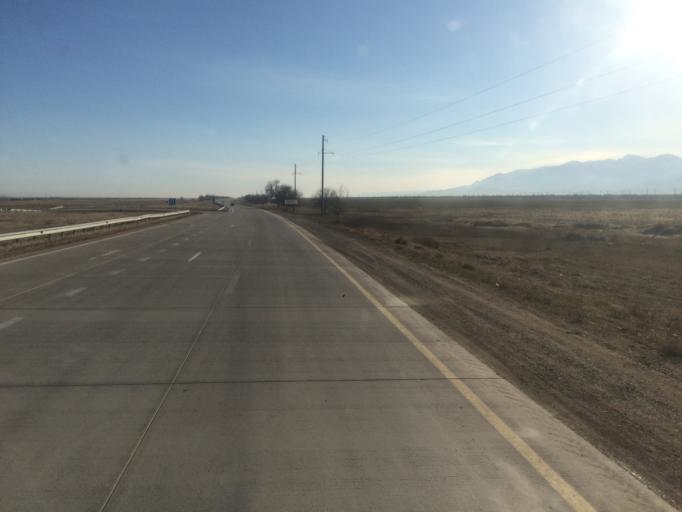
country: KZ
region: Zhambyl
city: Sarykemer
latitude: 43.0081
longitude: 71.8147
